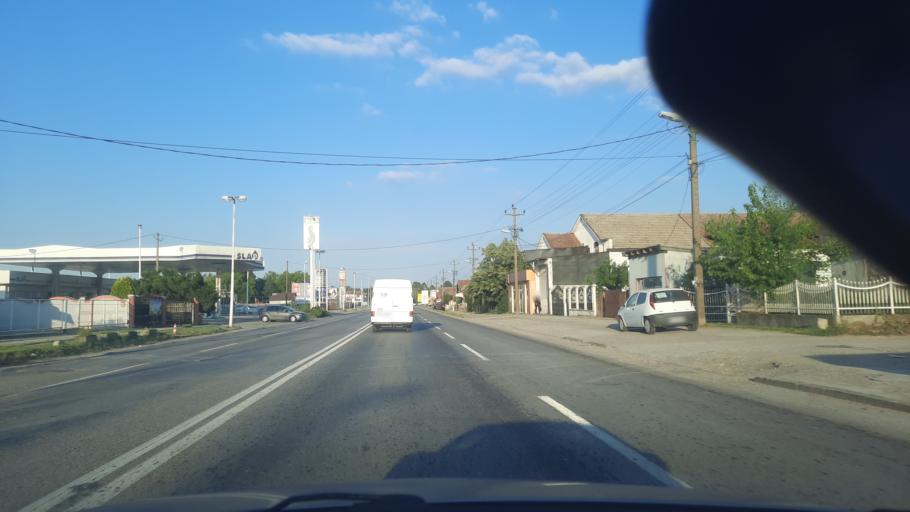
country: RS
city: Jelenca
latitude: 44.7391
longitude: 19.7294
